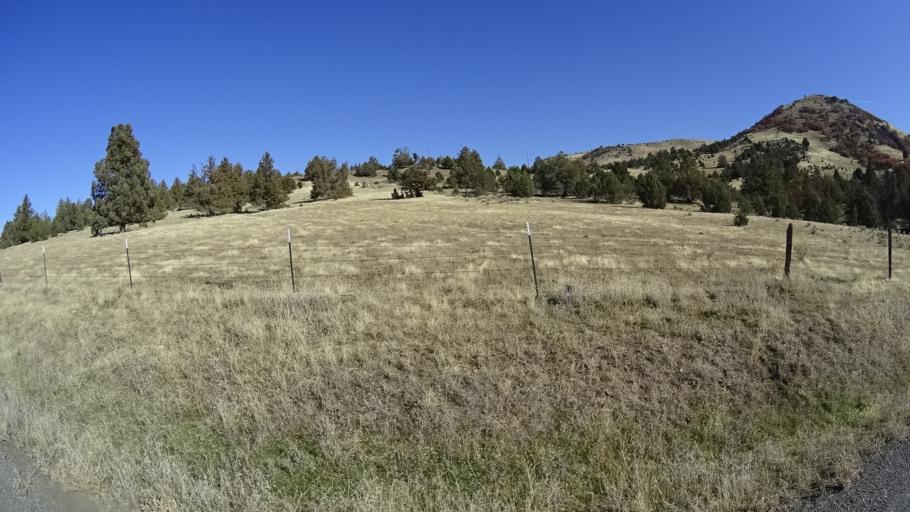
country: US
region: California
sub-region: Siskiyou County
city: Montague
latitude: 41.8020
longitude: -122.3695
